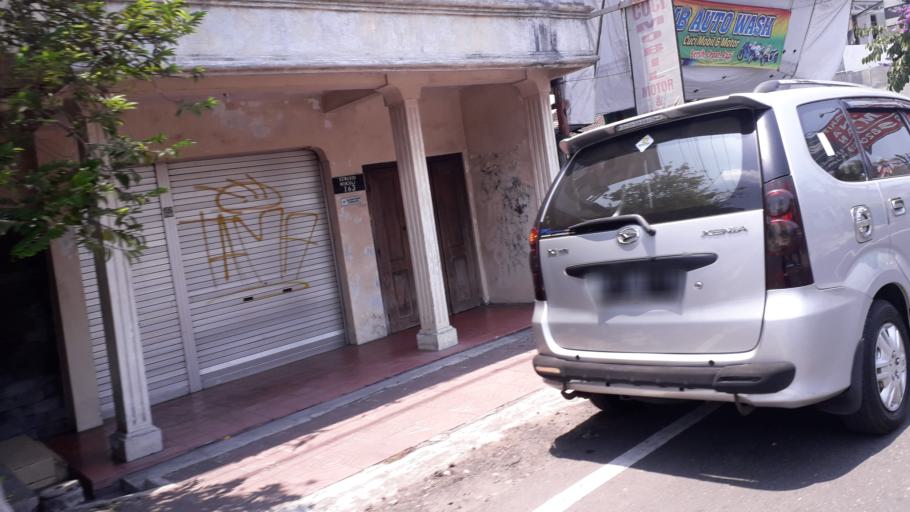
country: ID
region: Daerah Istimewa Yogyakarta
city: Yogyakarta
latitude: -7.7671
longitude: 110.3691
